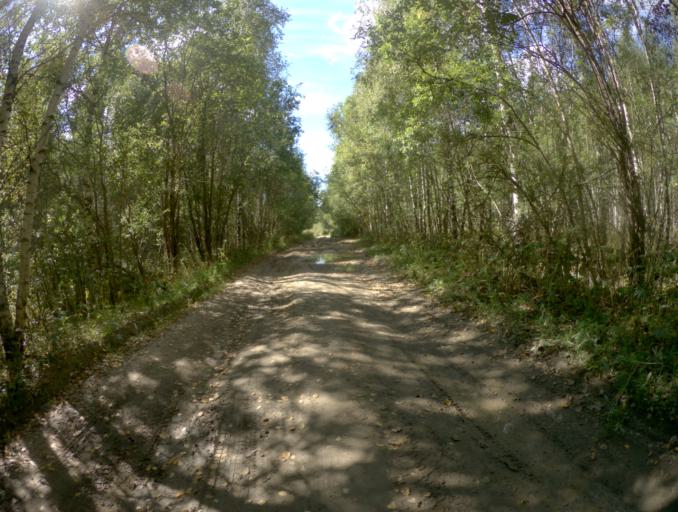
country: RU
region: Vladimir
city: Nikologory
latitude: 56.0237
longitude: 41.9404
